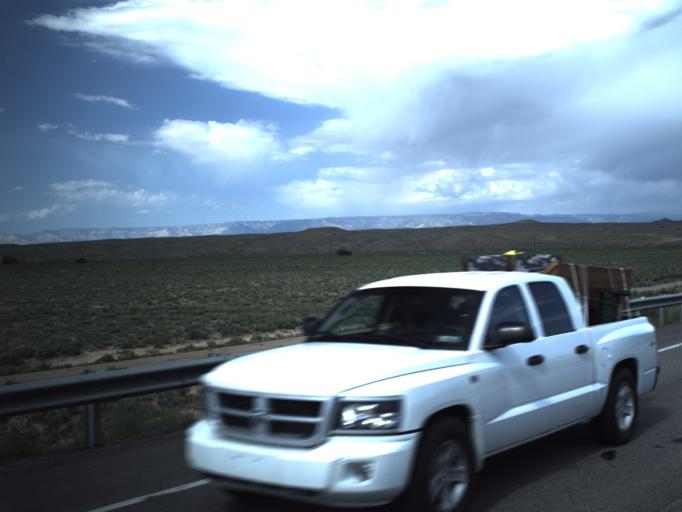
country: US
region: Utah
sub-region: Carbon County
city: East Carbon City
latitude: 39.5226
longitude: -110.5660
